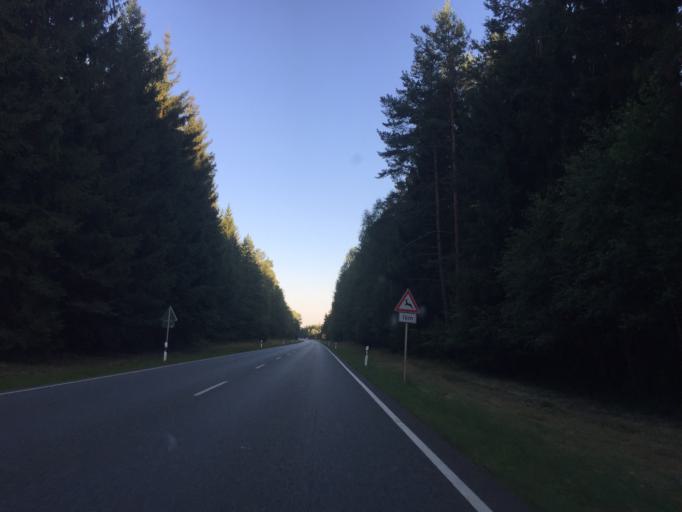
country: DE
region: Bavaria
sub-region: Upper Palatinate
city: Schwarzenbach
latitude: 49.7296
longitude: 11.9612
